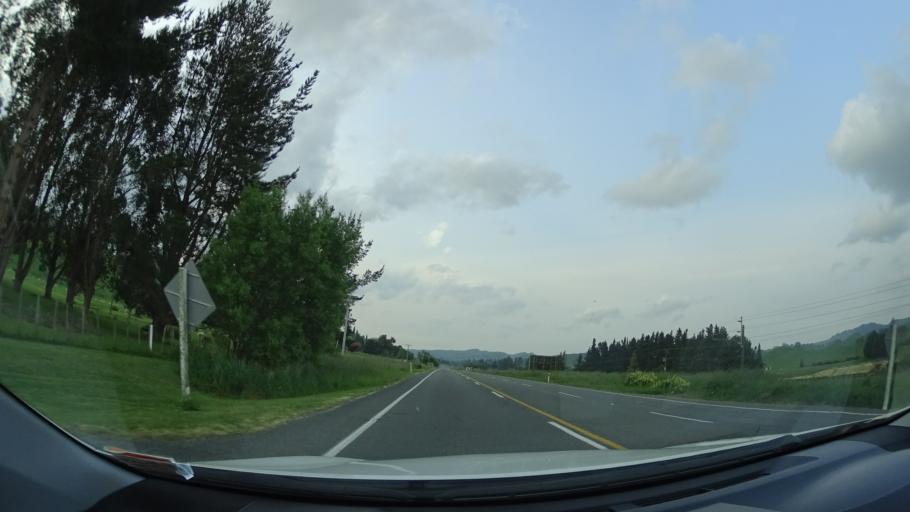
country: NZ
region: Manawatu-Wanganui
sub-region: Ruapehu District
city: Waiouru
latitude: -39.7267
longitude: 175.8425
